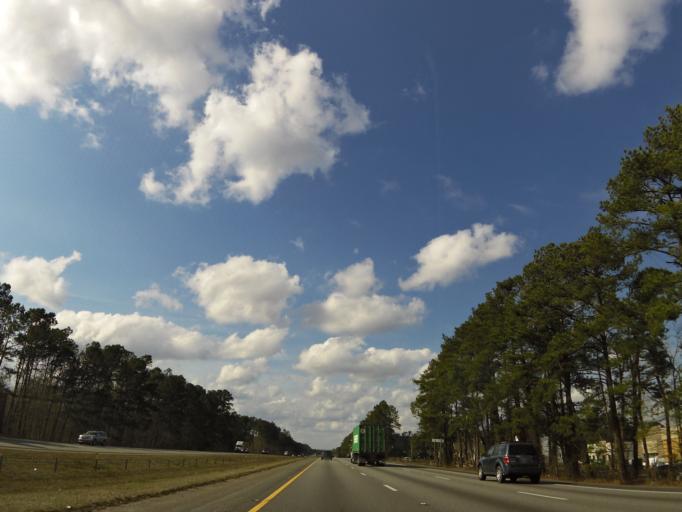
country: US
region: South Carolina
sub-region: Berkeley County
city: Sangaree
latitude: 33.0133
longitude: -80.1154
